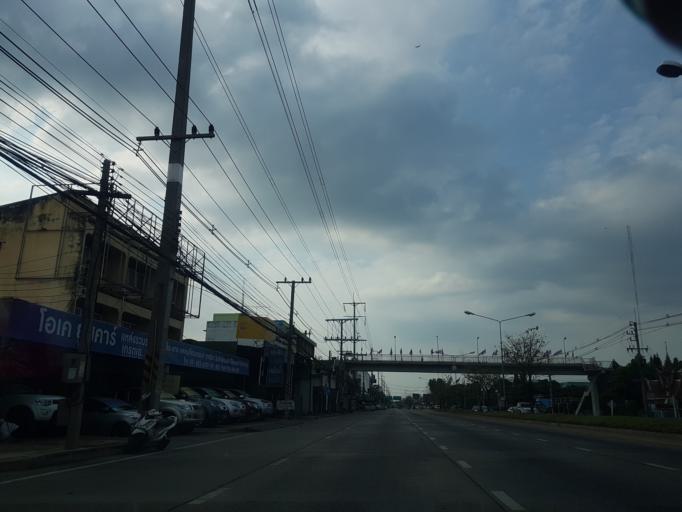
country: TH
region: Sara Buri
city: Phra Phutthabat
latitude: 14.7230
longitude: 100.8020
